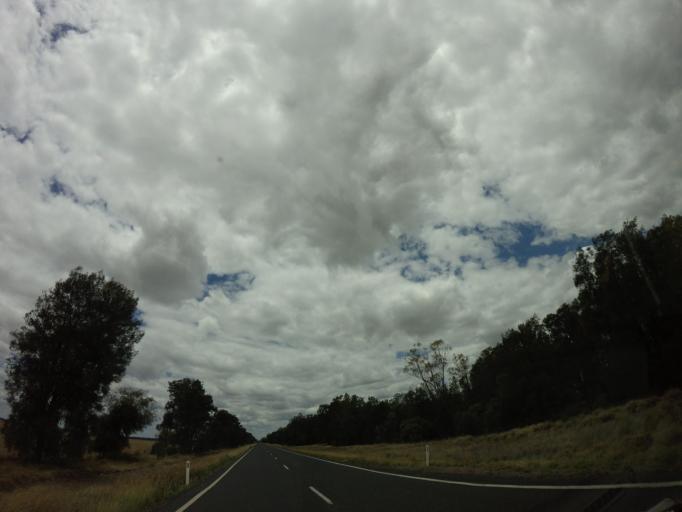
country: AU
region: Queensland
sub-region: Goondiwindi
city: Goondiwindi
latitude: -28.1676
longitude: 150.5521
